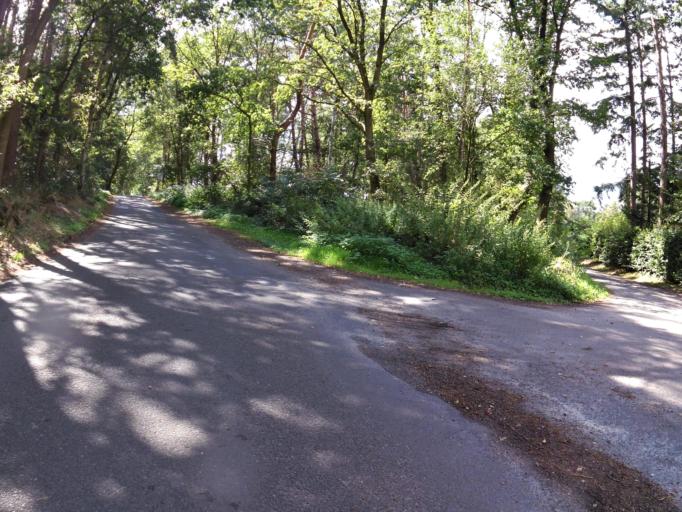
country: DE
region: Lower Saxony
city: Seedorf
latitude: 53.3320
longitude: 9.1971
